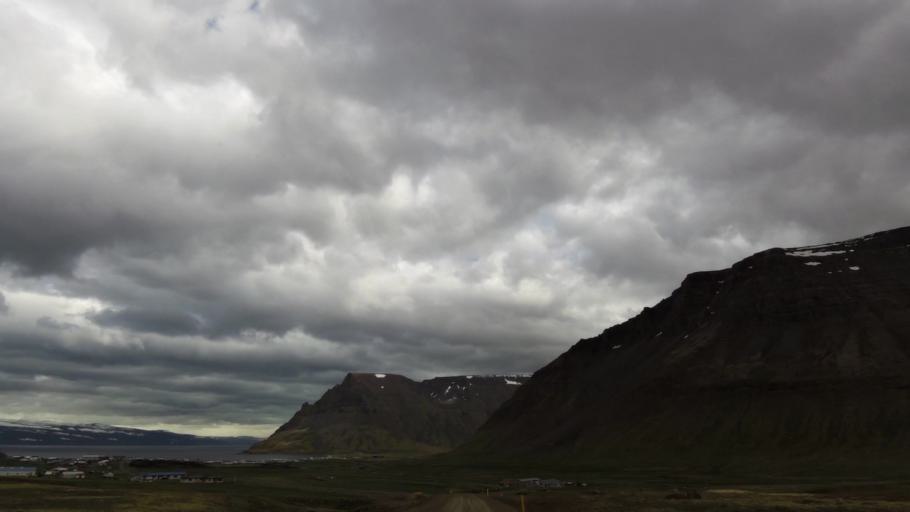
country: IS
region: Westfjords
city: Isafjoerdur
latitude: 66.1589
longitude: -23.2961
